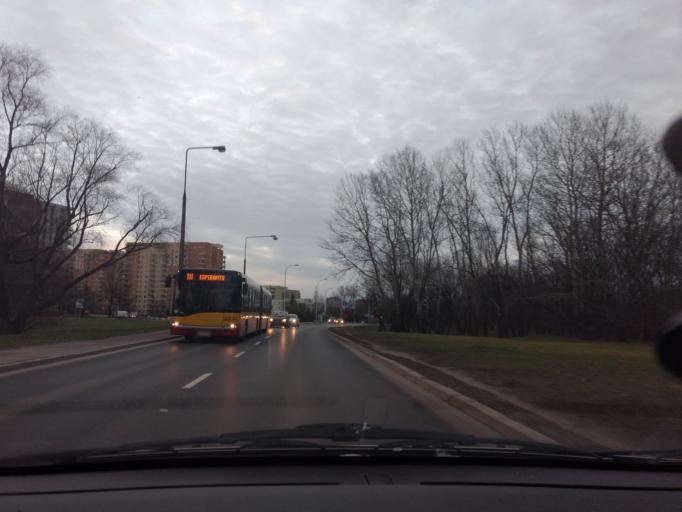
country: PL
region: Masovian Voivodeship
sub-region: Warszawa
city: Praga Poludnie
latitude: 52.2257
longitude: 21.0749
